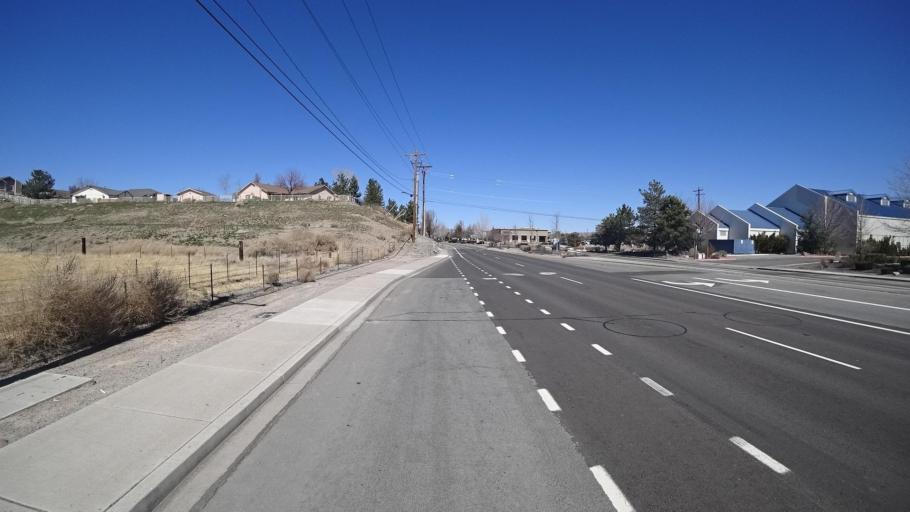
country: US
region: Nevada
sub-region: Washoe County
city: Sparks
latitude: 39.5776
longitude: -119.7242
